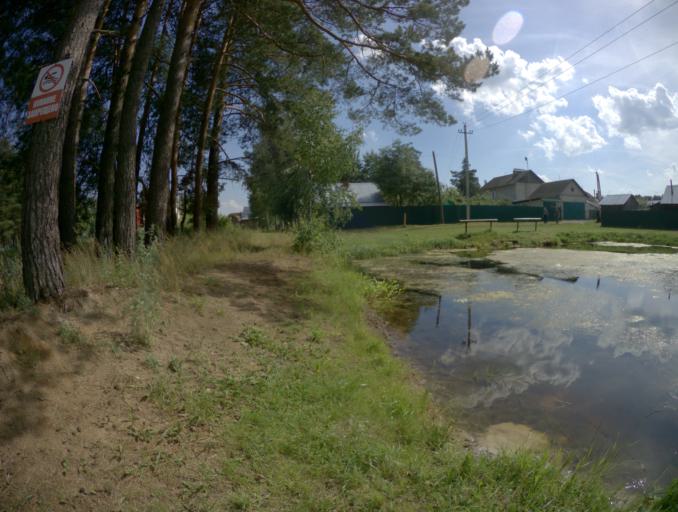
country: RU
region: Ivanovo
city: Talitsy
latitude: 56.5284
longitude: 42.3261
